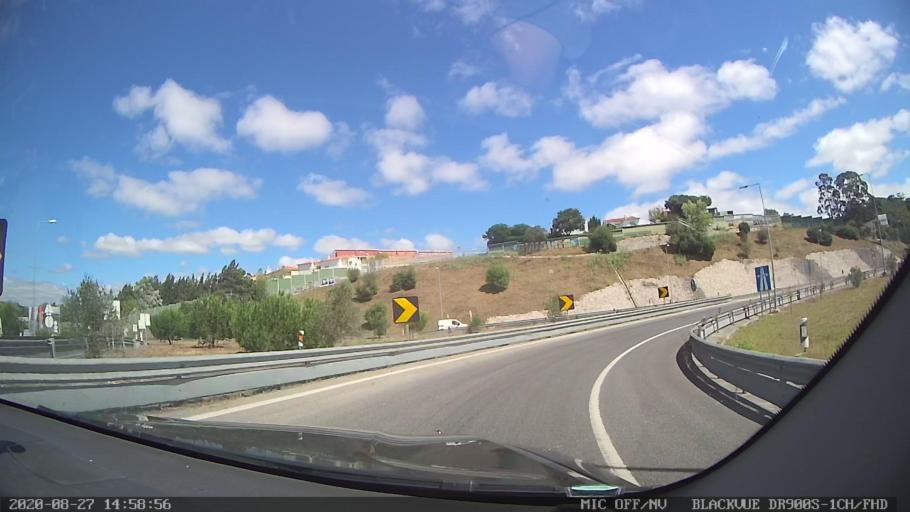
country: PT
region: Leiria
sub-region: Leiria
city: Leiria
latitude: 39.7479
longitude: -8.8205
